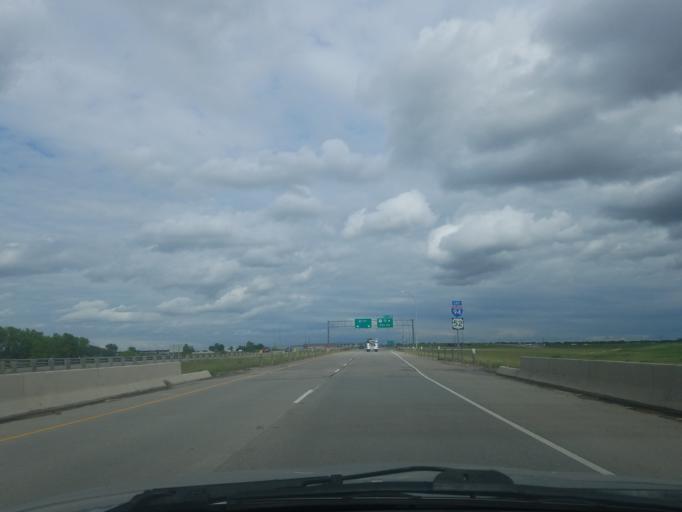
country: US
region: North Dakota
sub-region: Cass County
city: West Fargo
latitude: 46.8776
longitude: -96.9593
